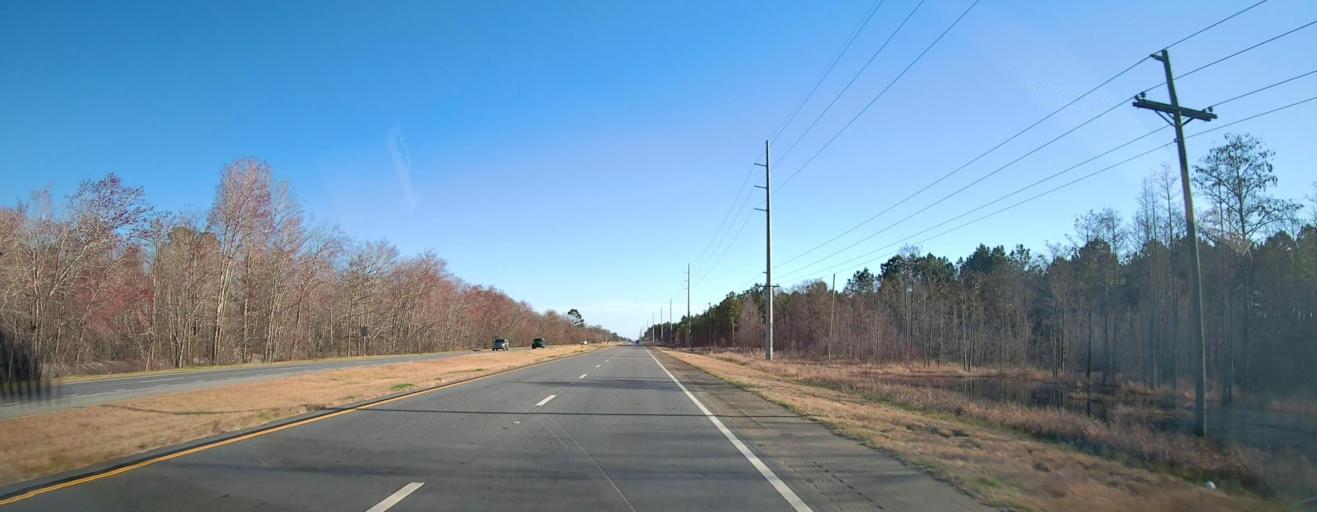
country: US
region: Georgia
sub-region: Lee County
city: Leesburg
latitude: 31.8816
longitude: -84.2432
